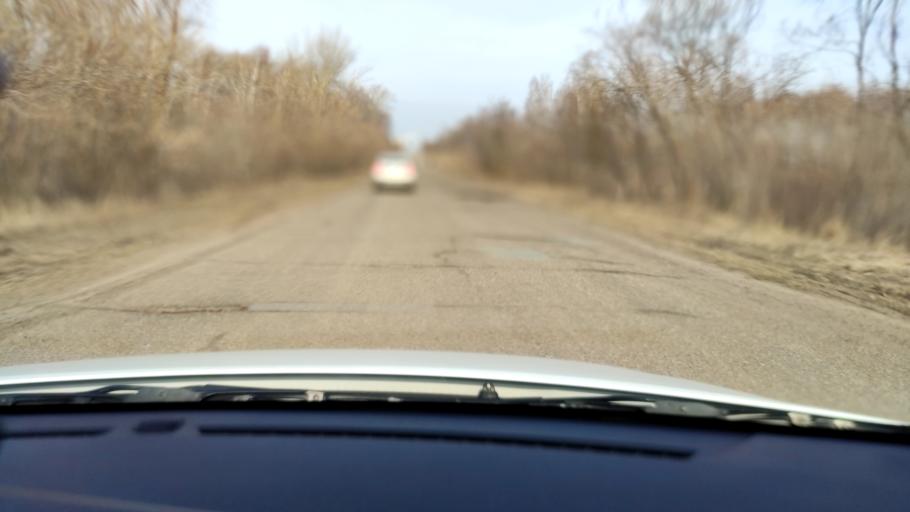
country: RU
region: Tatarstan
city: Stolbishchi
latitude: 55.7209
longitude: 49.2102
